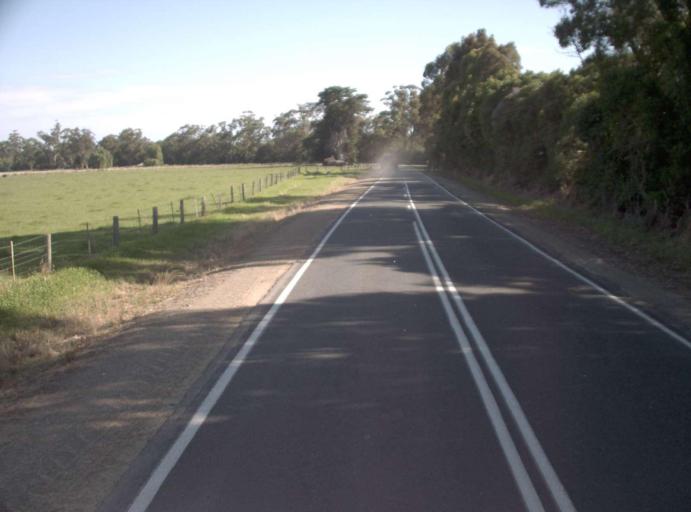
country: AU
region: Victoria
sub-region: East Gippsland
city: Lakes Entrance
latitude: -37.7342
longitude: 148.5050
